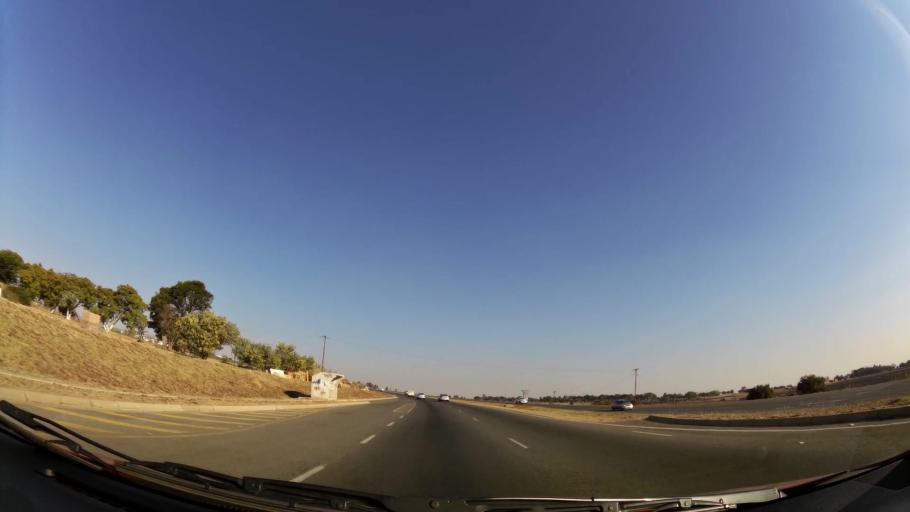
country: ZA
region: Gauteng
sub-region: West Rand District Municipality
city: Muldersdriseloop
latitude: -25.9902
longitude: 27.9249
